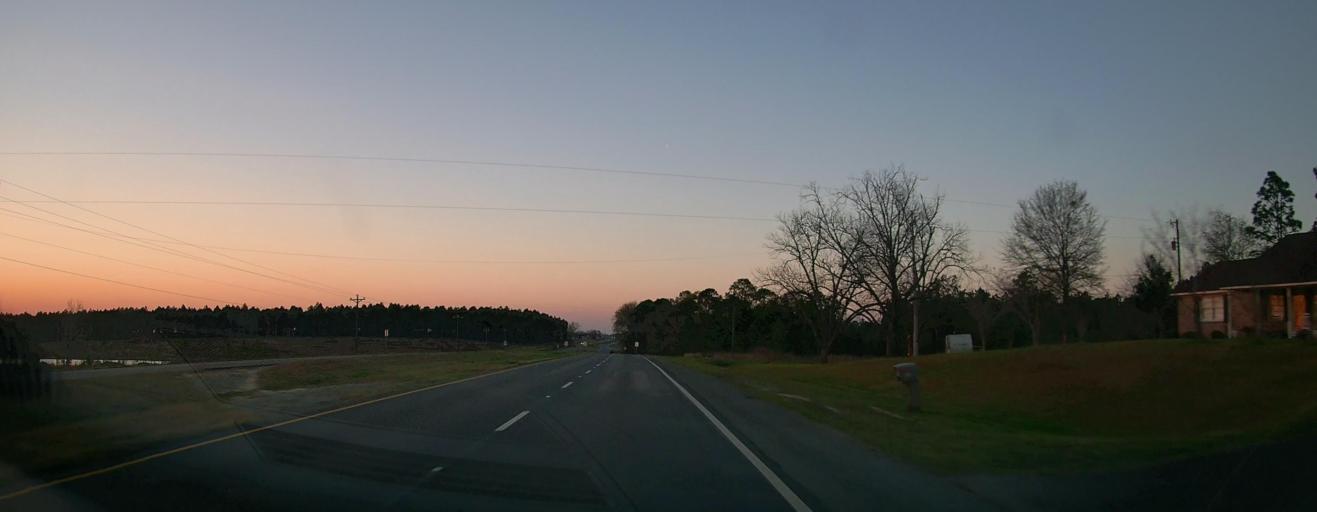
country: US
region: Georgia
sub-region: Dodge County
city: Eastman
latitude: 32.1581
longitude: -83.1469
